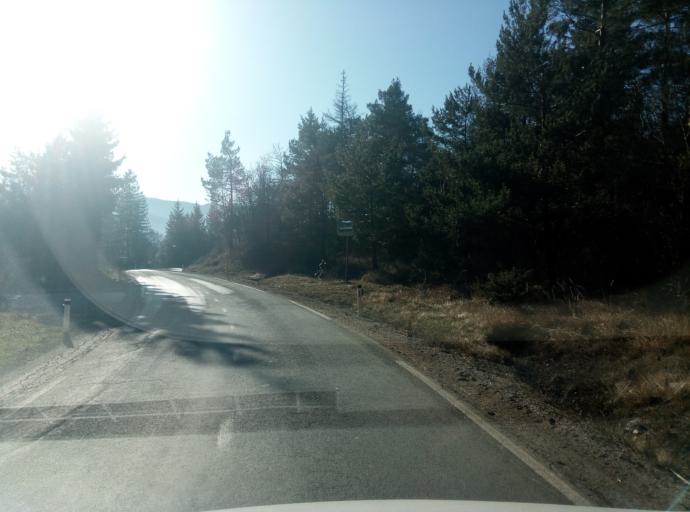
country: SI
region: Bloke
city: Nova Vas
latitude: 45.7642
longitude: 14.4336
